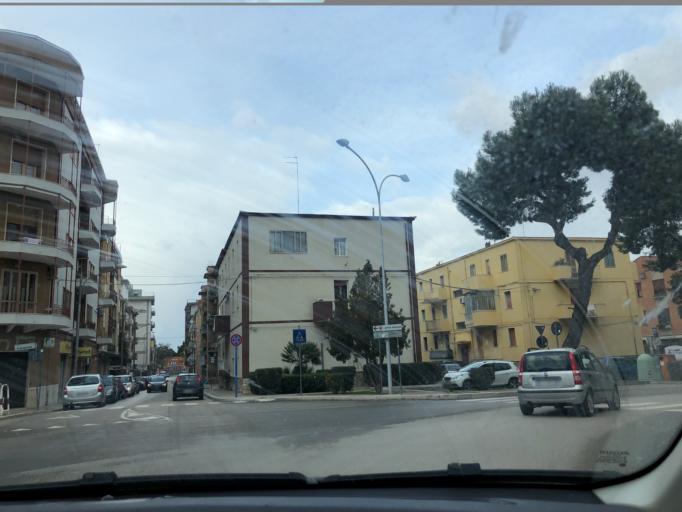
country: IT
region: Apulia
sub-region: Provincia di Foggia
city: Lucera
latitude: 41.5110
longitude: 15.3316
